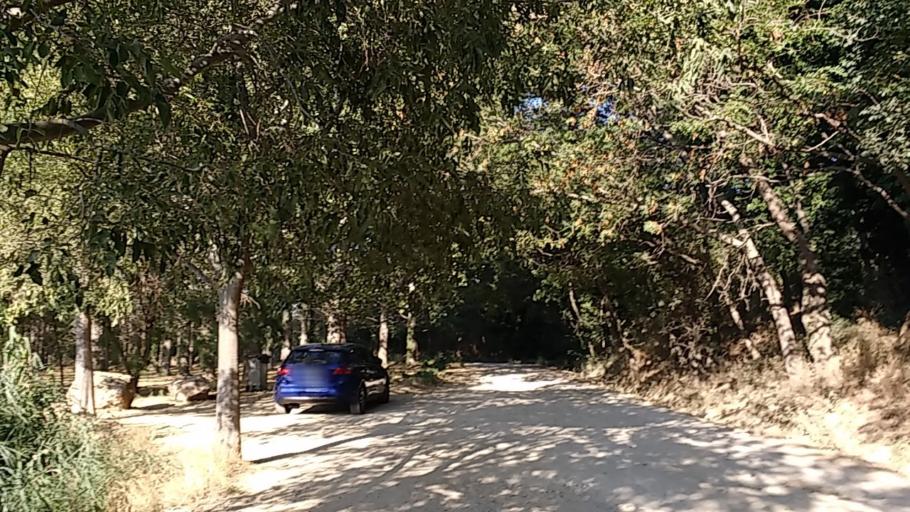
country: FR
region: Languedoc-Roussillon
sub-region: Departement des Pyrenees-Orientales
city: Palau-del-Vidre
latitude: 42.5799
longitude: 2.9610
